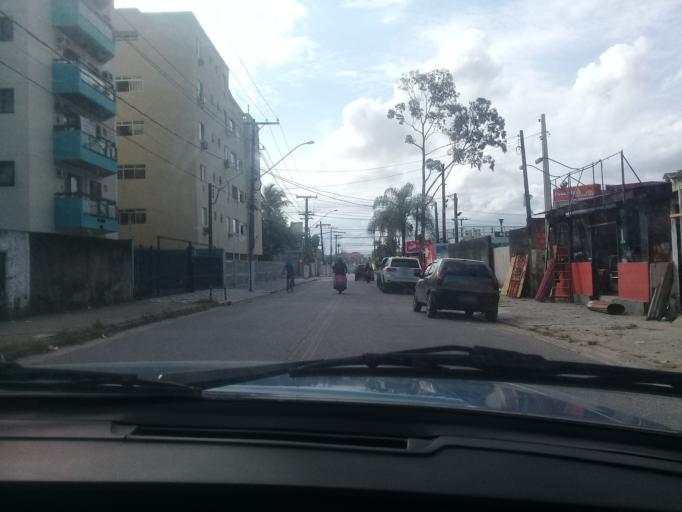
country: BR
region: Sao Paulo
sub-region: Guaruja
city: Guaruja
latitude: -24.0046
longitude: -46.2728
